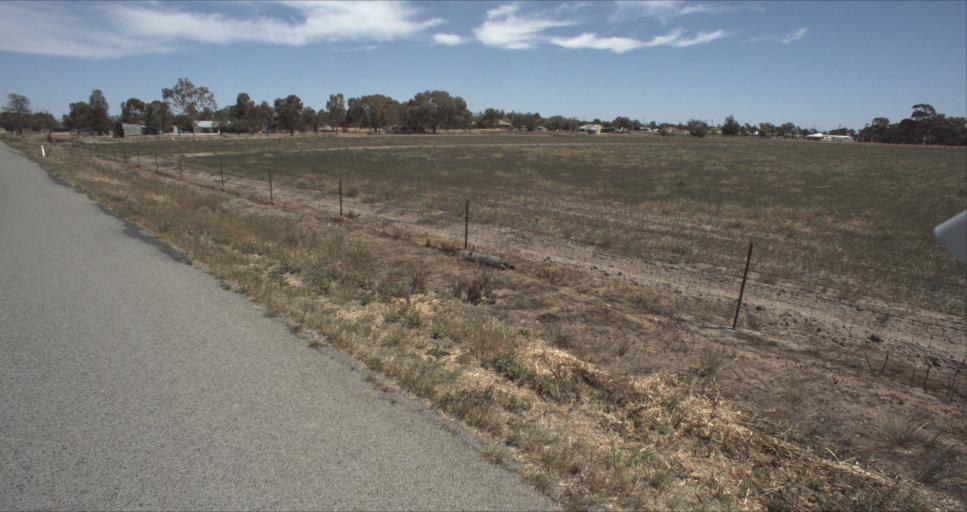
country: AU
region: New South Wales
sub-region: Leeton
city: Leeton
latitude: -34.5982
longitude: 146.4161
